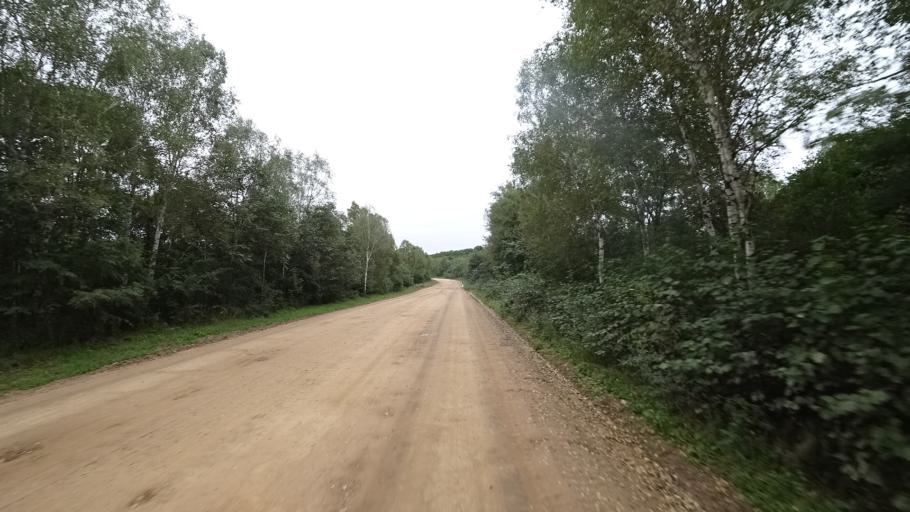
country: RU
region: Primorskiy
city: Rettikhovka
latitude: 44.1750
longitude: 132.7997
